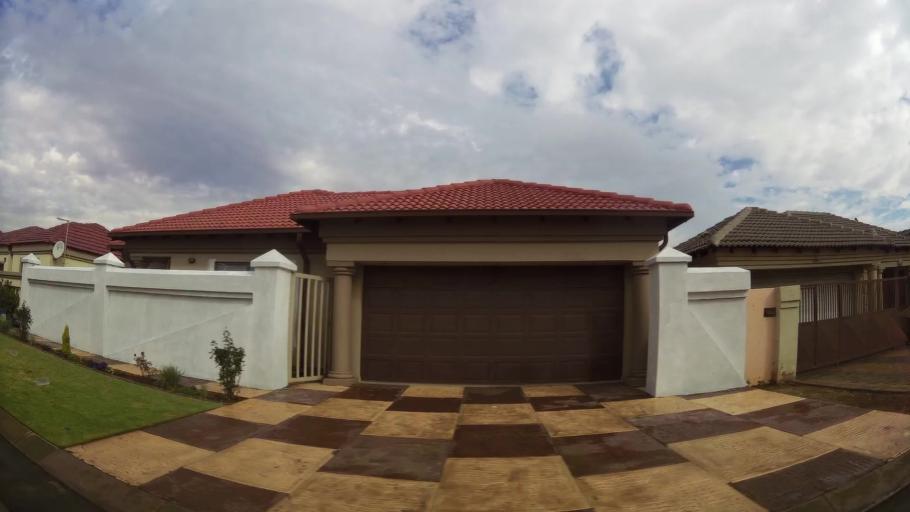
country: ZA
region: Gauteng
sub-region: Ekurhuleni Metropolitan Municipality
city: Germiston
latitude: -26.3332
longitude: 28.1944
